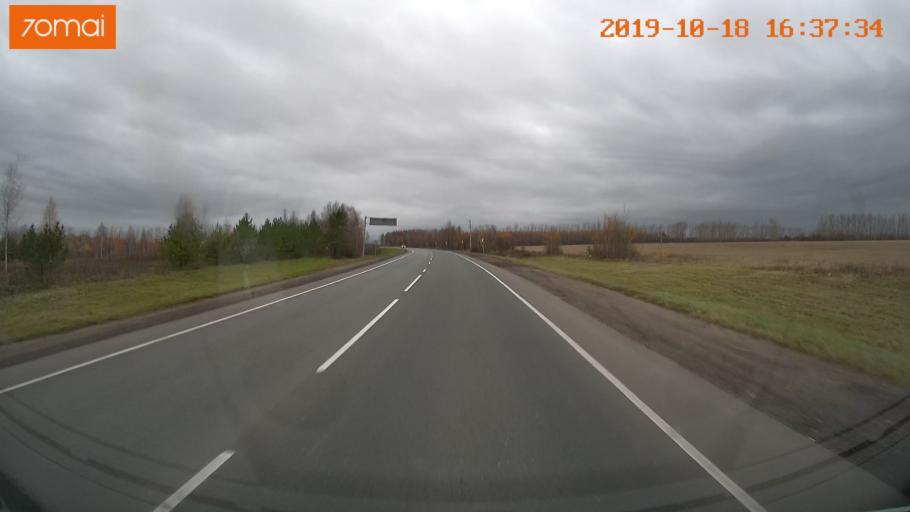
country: RU
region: Vladimir
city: Suzdal'
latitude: 56.4237
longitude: 40.4767
